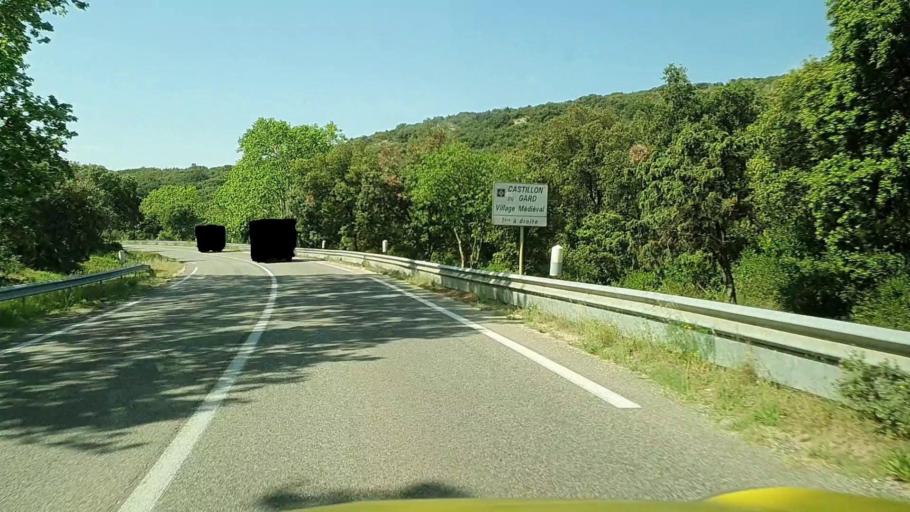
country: FR
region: Languedoc-Roussillon
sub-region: Departement du Gard
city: Castillon-du-Gard
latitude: 43.9821
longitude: 4.5747
